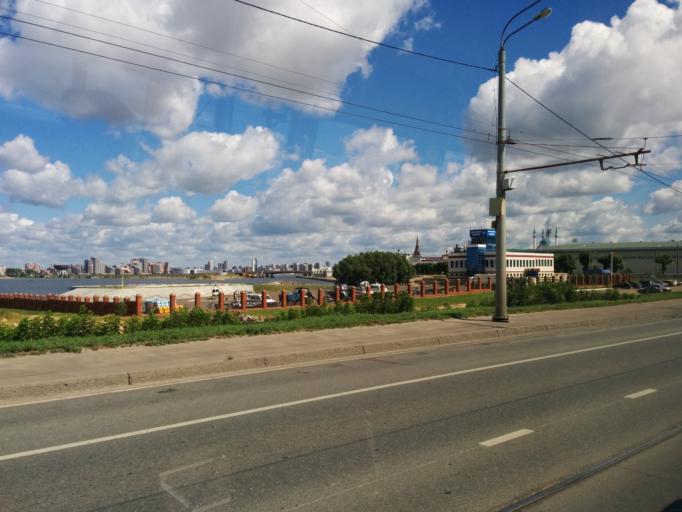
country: RU
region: Tatarstan
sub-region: Gorod Kazan'
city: Kazan
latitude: 55.7963
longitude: 49.0885
